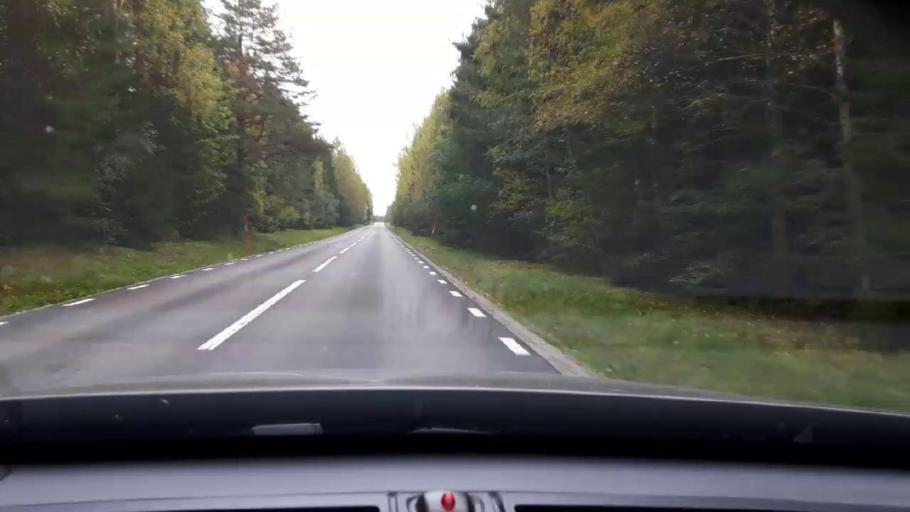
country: SE
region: Dalarna
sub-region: Ludvika Kommun
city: Grangesberg
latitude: 60.2320
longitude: 15.0348
